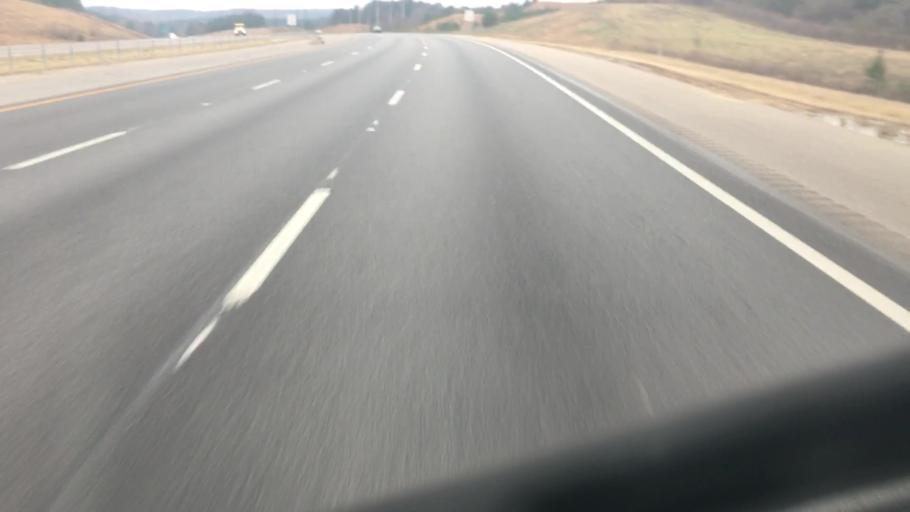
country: US
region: Alabama
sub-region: Jefferson County
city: Fultondale
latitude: 33.5840
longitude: -86.8295
